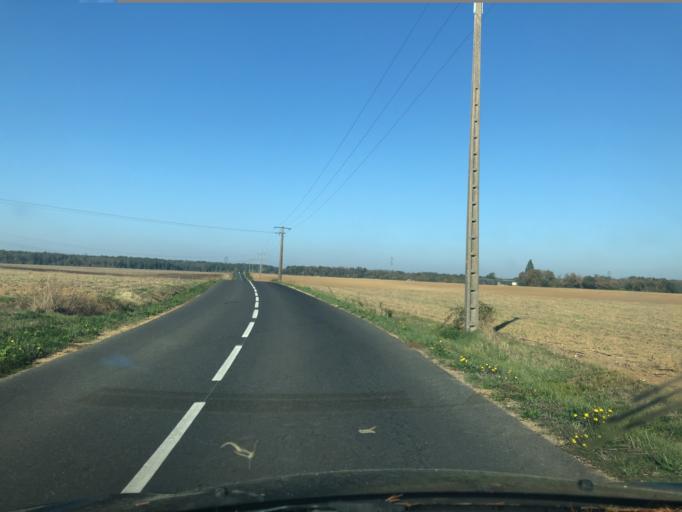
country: FR
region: Centre
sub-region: Departement d'Indre-et-Loire
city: Rouziers-de-Touraine
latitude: 47.5231
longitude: 0.6450
